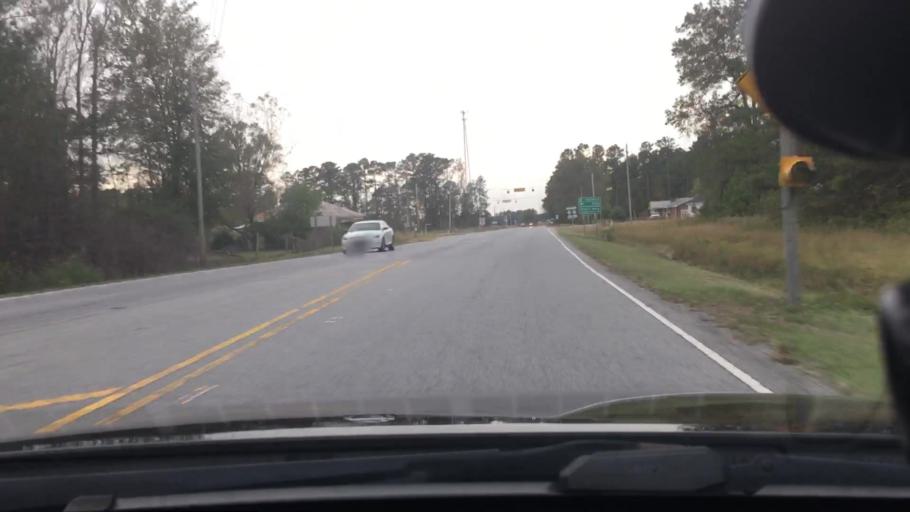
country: US
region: North Carolina
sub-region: Craven County
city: Vanceboro
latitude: 35.4172
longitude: -77.2555
